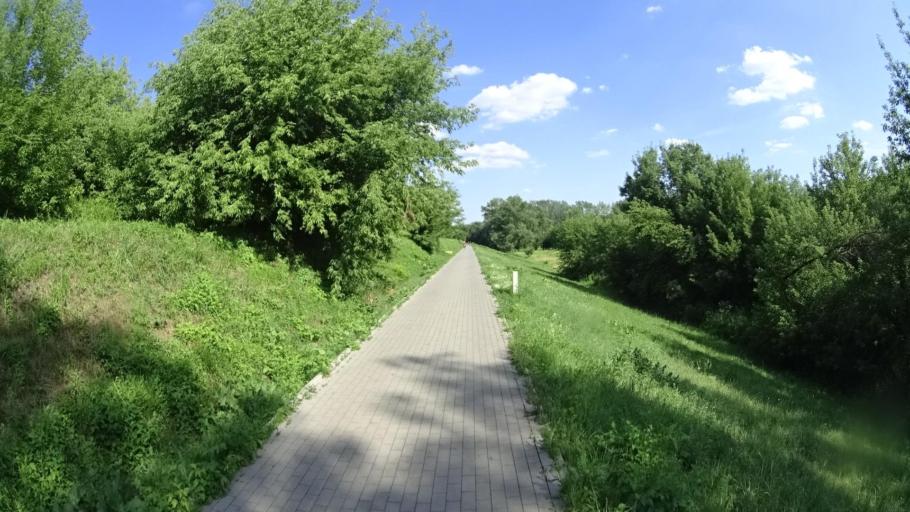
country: PL
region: Masovian Voivodeship
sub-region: Warszawa
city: Bialoleka
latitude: 52.3014
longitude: 20.9691
